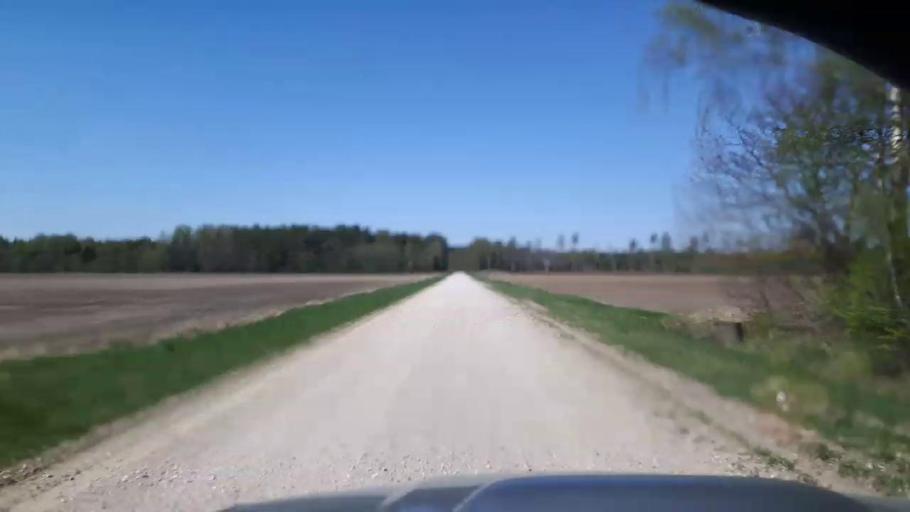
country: EE
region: Paernumaa
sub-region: Tootsi vald
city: Tootsi
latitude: 58.4714
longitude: 24.7658
